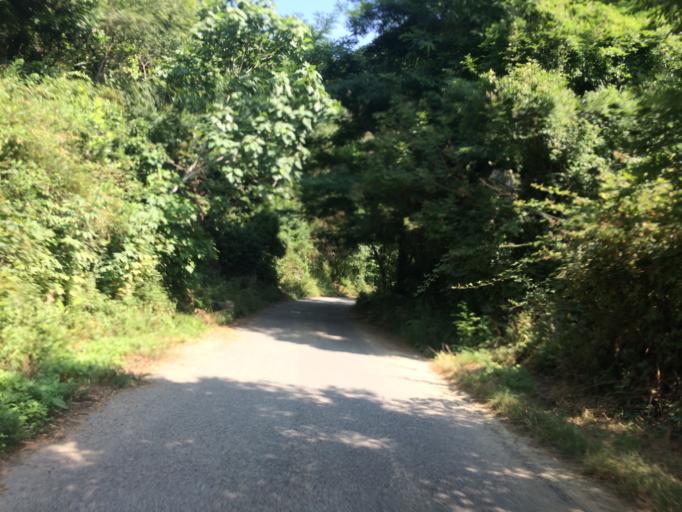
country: IT
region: Liguria
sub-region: Provincia di Genova
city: Sciarborasca
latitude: 44.4049
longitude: 8.5758
